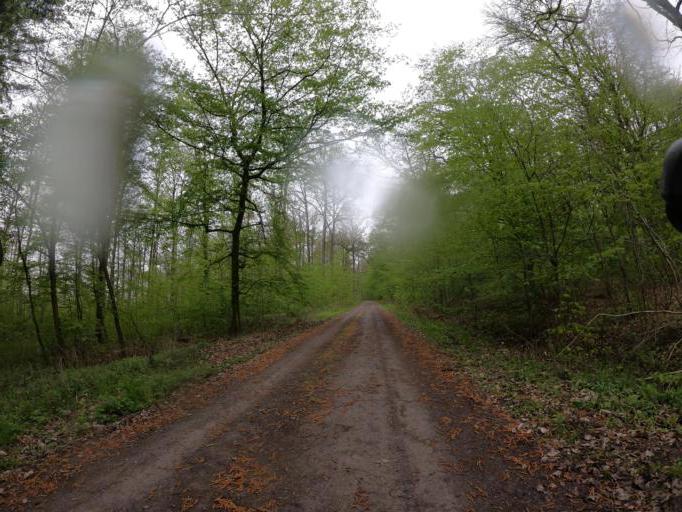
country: DE
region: Baden-Wuerttemberg
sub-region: Karlsruhe Region
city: Illingen
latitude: 48.9735
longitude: 8.8940
